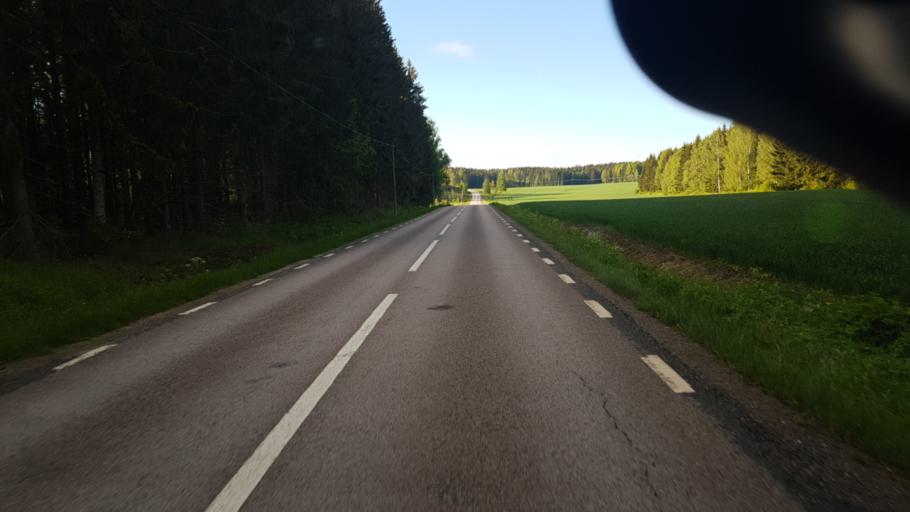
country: SE
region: Vaermland
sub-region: Arvika Kommun
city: Arvika
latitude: 59.5976
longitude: 12.5367
